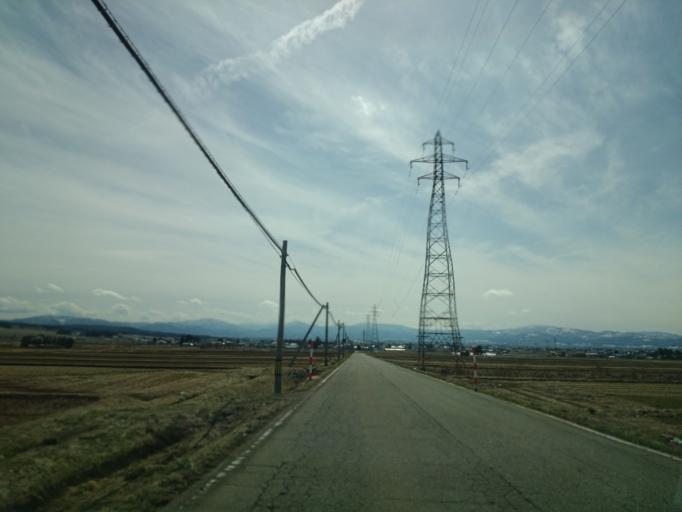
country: JP
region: Fukushima
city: Kitakata
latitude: 37.6534
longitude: 139.9118
